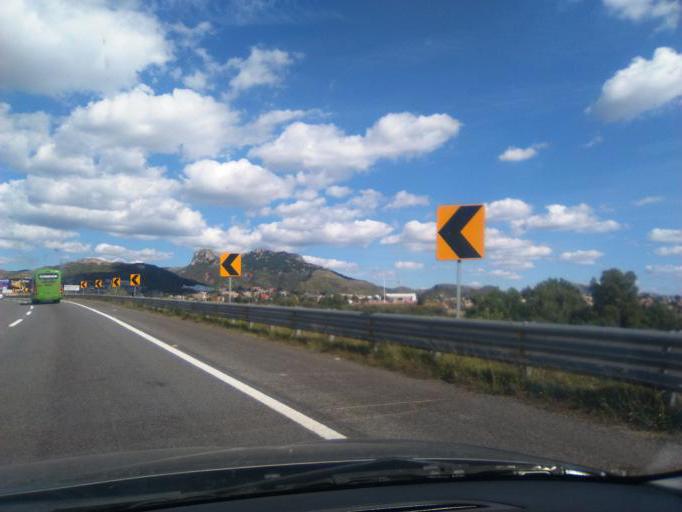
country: MX
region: Guanajuato
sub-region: Guanajuato
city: San Jose de Cervera
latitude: 20.9773
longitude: -101.2949
